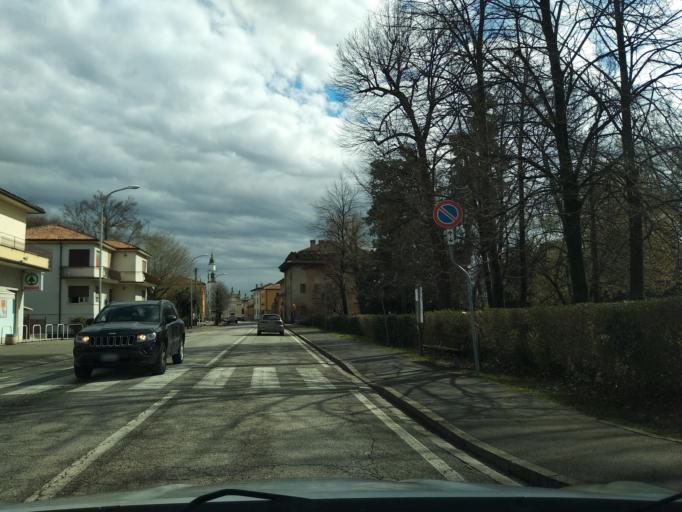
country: IT
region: Veneto
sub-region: Provincia di Vicenza
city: Monticello Conte Otto
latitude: 45.5946
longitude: 11.5823
